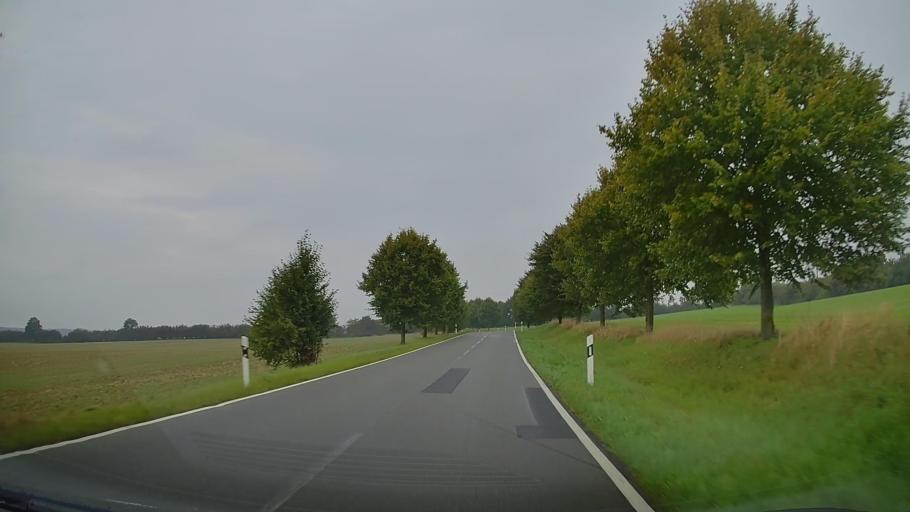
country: DE
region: Mecklenburg-Vorpommern
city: Kalkhorst
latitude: 53.9777
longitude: 11.0481
